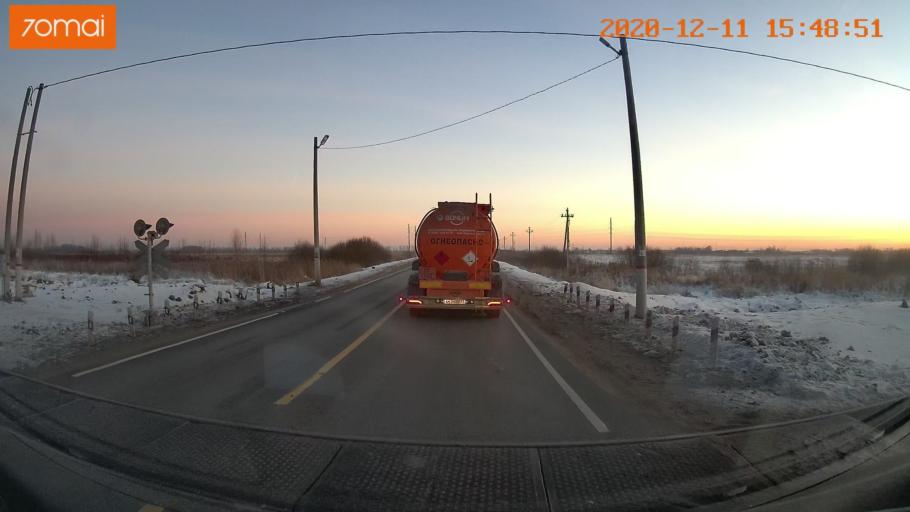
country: RU
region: Ivanovo
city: Novo-Talitsy
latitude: 56.9913
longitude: 40.8704
